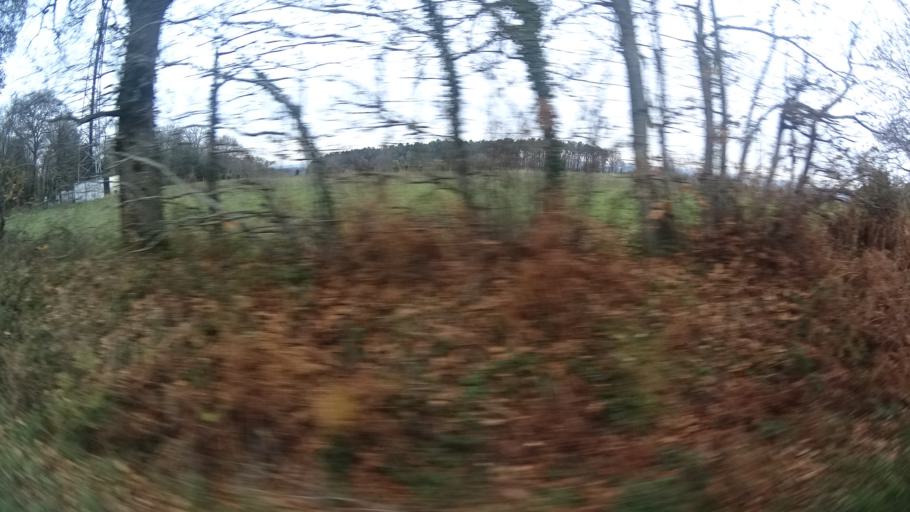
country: FR
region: Pays de la Loire
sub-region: Departement de la Loire-Atlantique
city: Avessac
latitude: 47.6467
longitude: -2.0003
